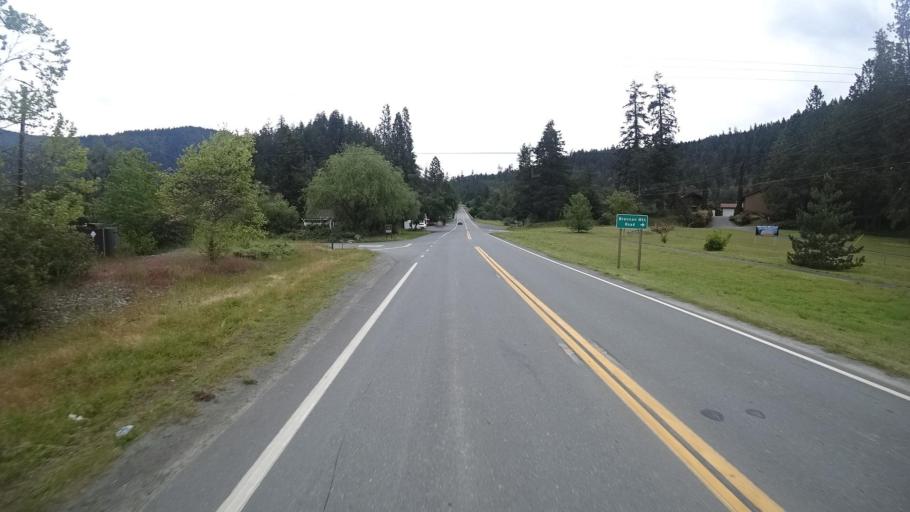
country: US
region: California
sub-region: Humboldt County
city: Willow Creek
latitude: 40.9451
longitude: -123.6344
